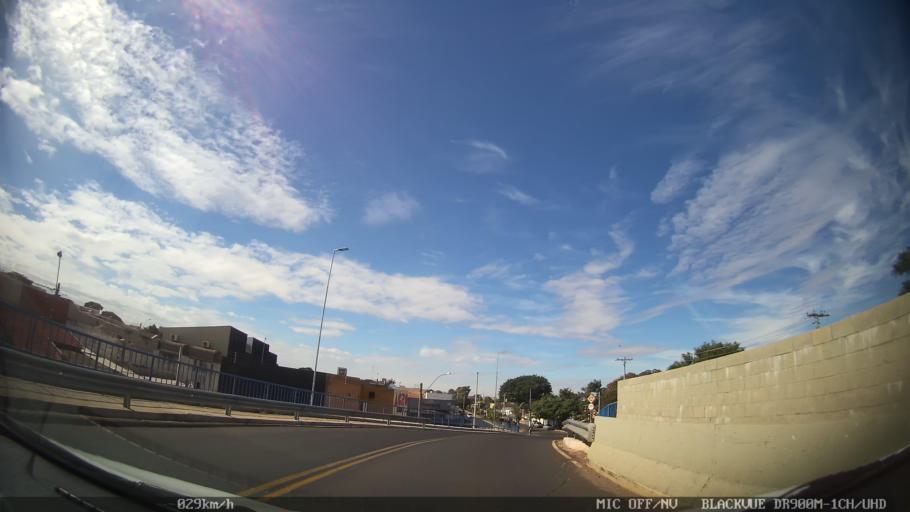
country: BR
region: Sao Paulo
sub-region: Bady Bassitt
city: Bady Bassitt
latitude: -20.8213
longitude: -49.4956
